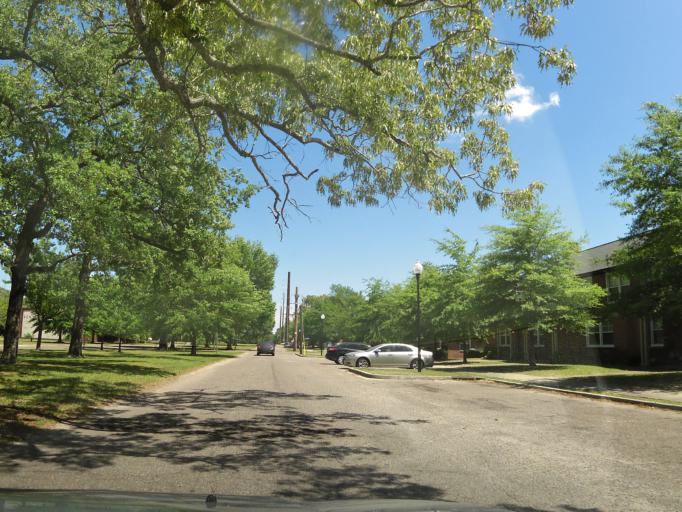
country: US
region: South Carolina
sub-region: Aiken County
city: Aiken
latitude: 33.5605
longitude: -81.7125
